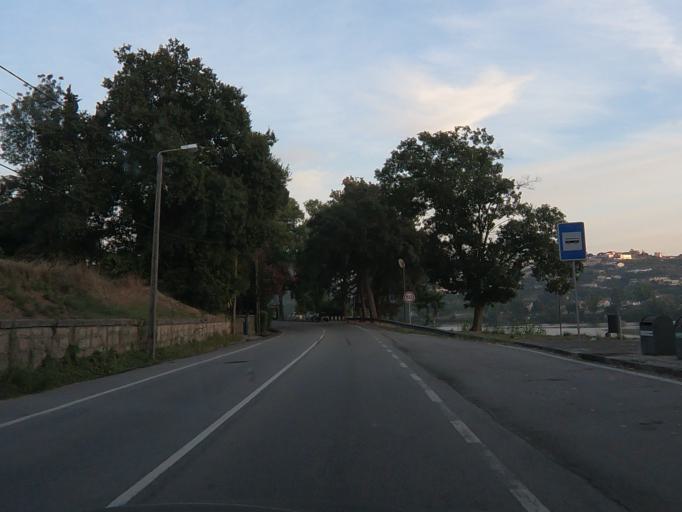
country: PT
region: Porto
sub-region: Gondomar
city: Valbom
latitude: 41.1277
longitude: -8.5661
